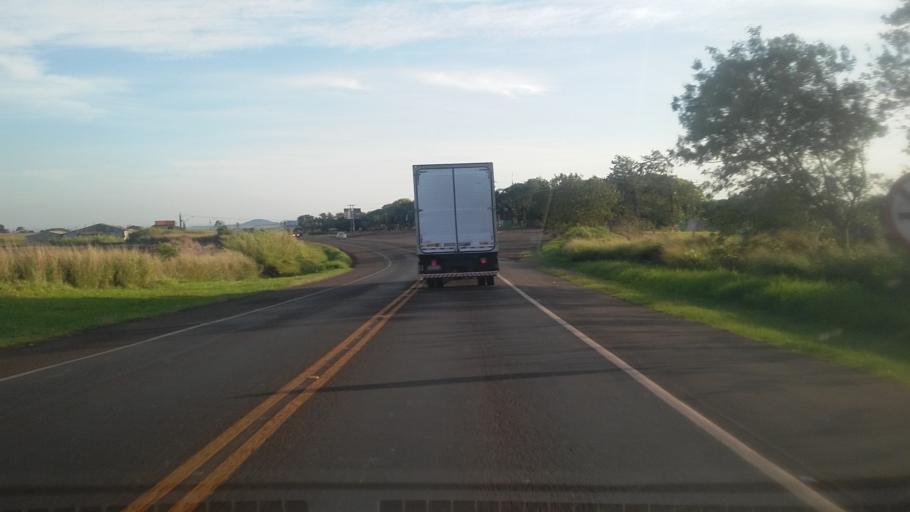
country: BR
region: Parana
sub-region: Bandeirantes
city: Bandeirantes
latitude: -23.1677
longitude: -50.6114
